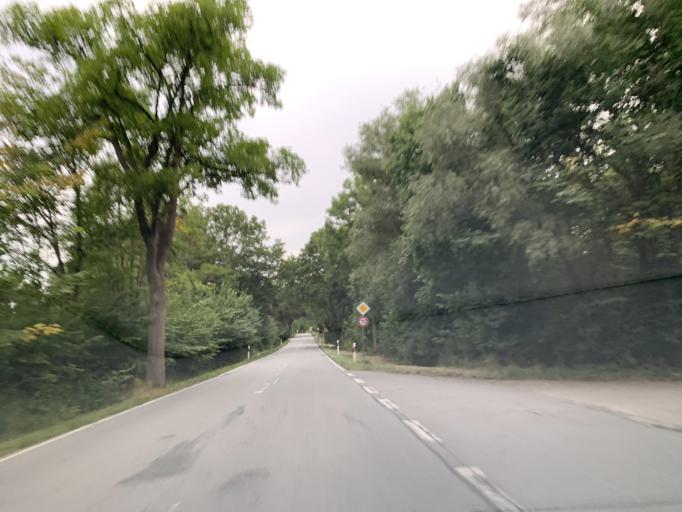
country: DE
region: Mecklenburg-Vorpommern
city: Neverin
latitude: 53.5988
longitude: 13.3301
